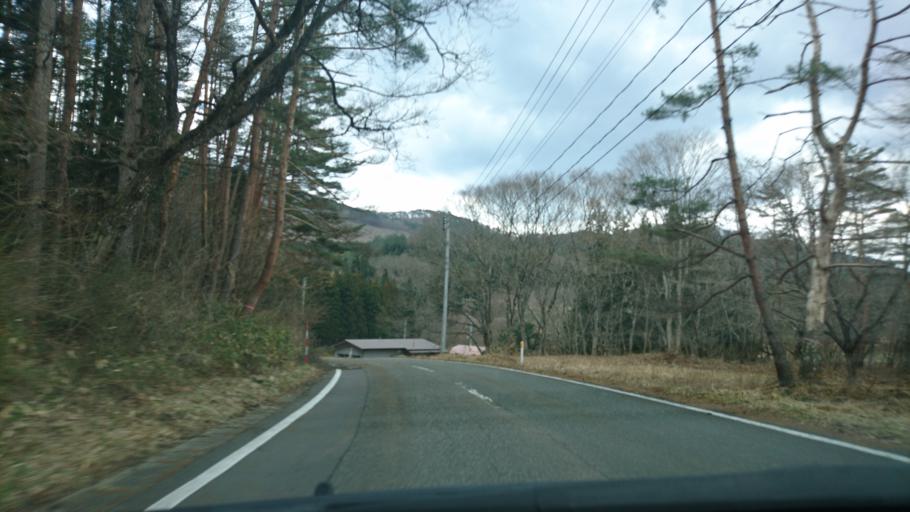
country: JP
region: Iwate
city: Tono
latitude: 39.3445
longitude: 141.3346
